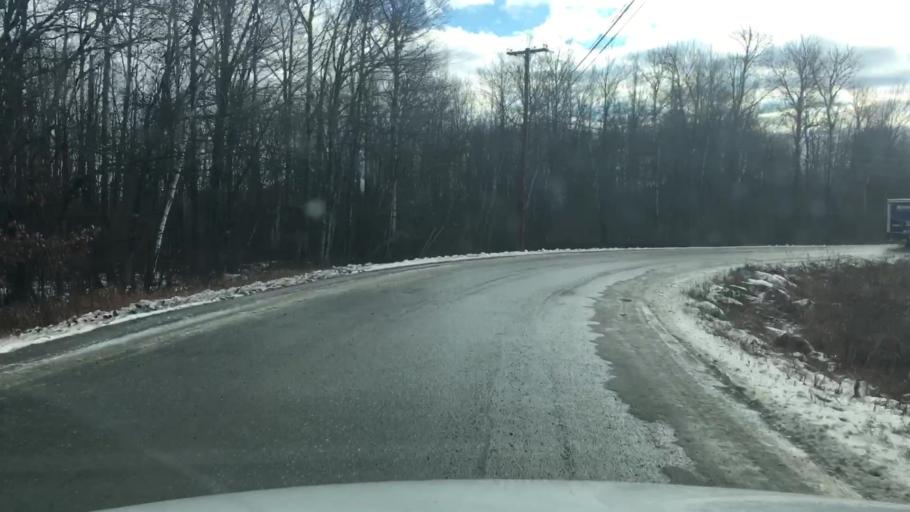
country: US
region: Maine
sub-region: Penobscot County
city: Brewer
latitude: 44.7291
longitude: -68.7558
